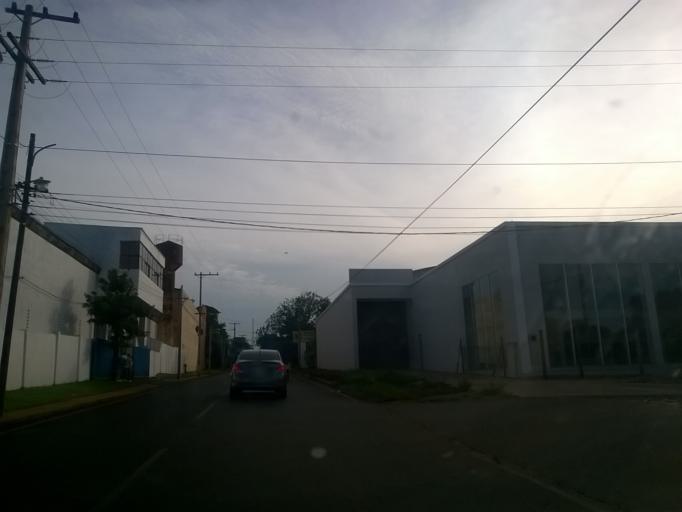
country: PY
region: Alto Parana
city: Ciudad del Este
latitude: -25.4995
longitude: -54.6330
